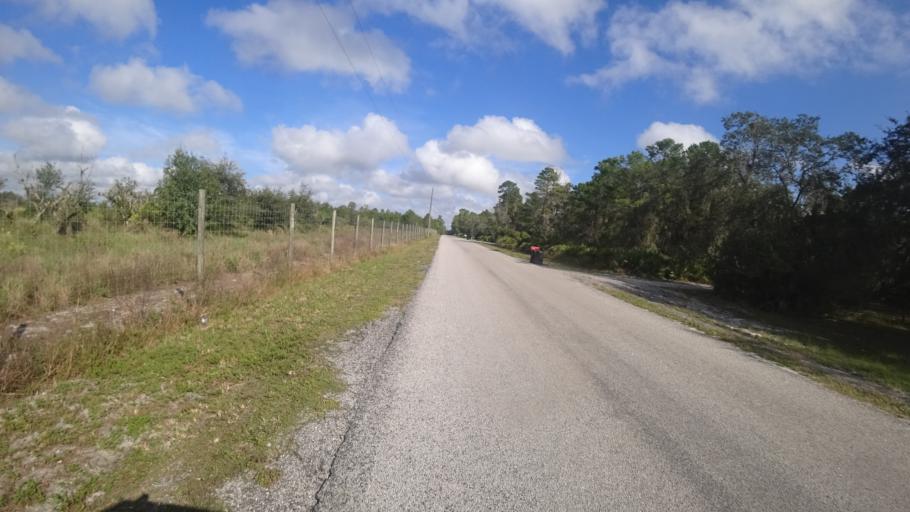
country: US
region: Florida
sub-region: Hillsborough County
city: Wimauma
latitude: 27.4518
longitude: -82.1369
